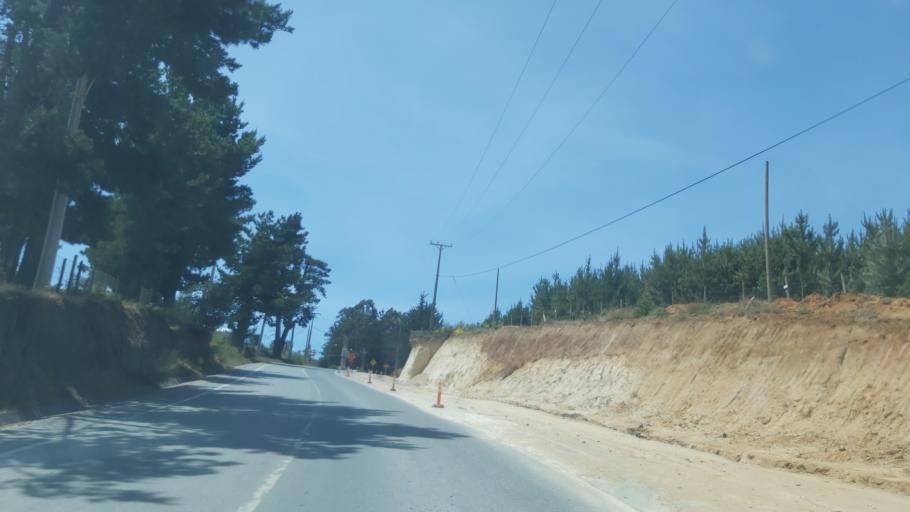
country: CL
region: Maule
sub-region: Provincia de Talca
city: Constitucion
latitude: -35.4424
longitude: -72.4583
